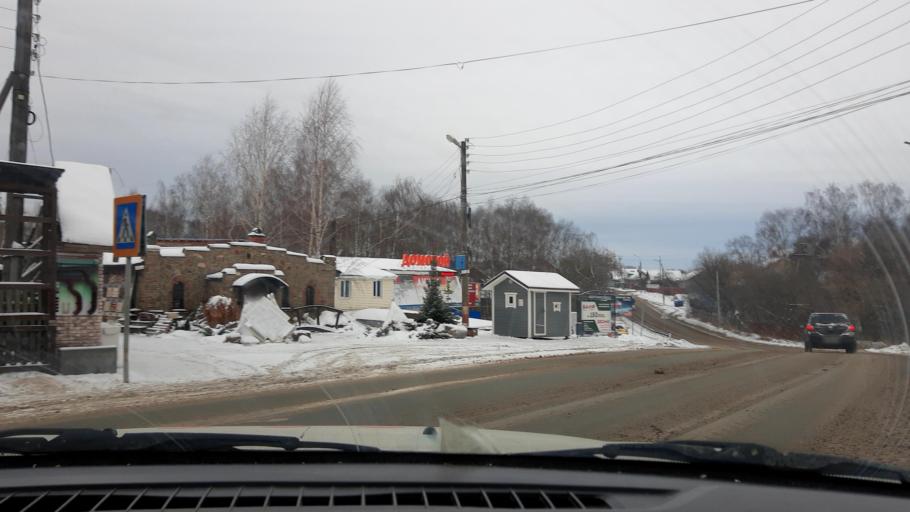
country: RU
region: Nizjnij Novgorod
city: Gorodets
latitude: 56.6575
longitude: 43.4839
